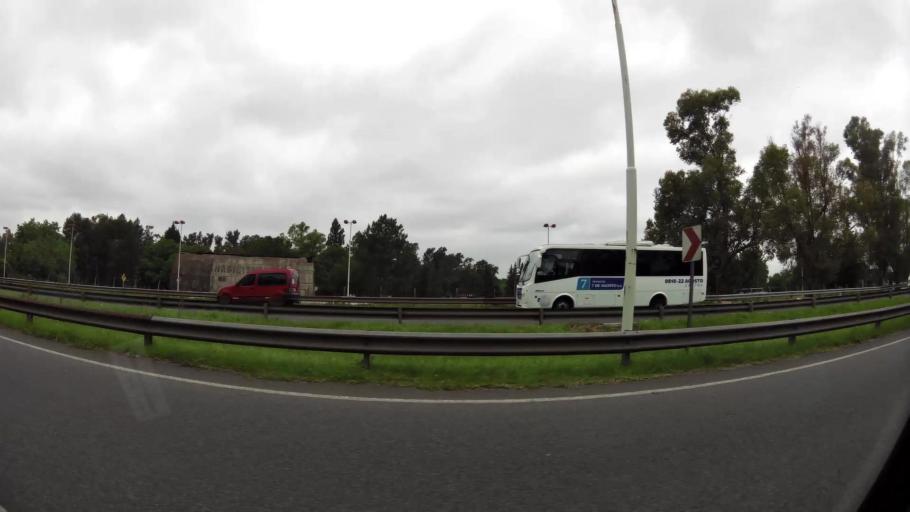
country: AR
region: Buenos Aires
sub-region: Partido de Ezeiza
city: Ezeiza
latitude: -34.8110
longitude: -58.5114
